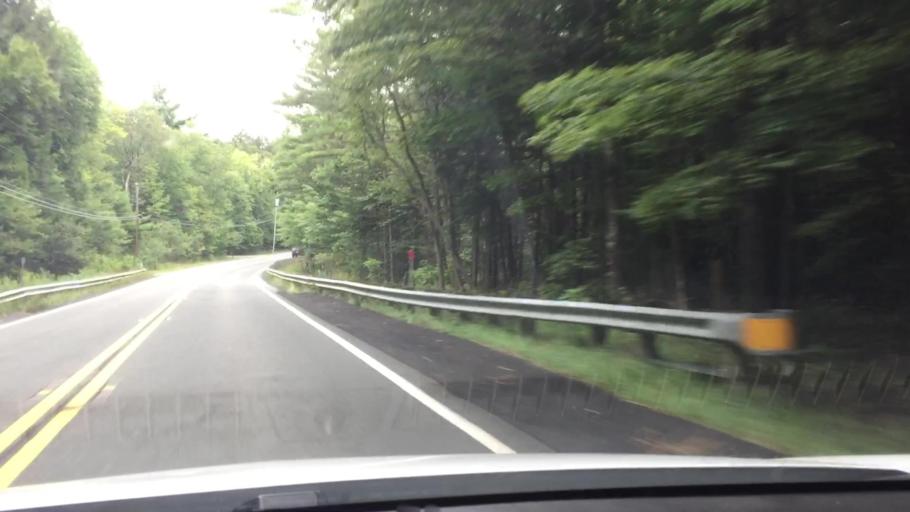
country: US
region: Massachusetts
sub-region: Berkshire County
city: Becket
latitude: 42.3558
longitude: -73.0988
